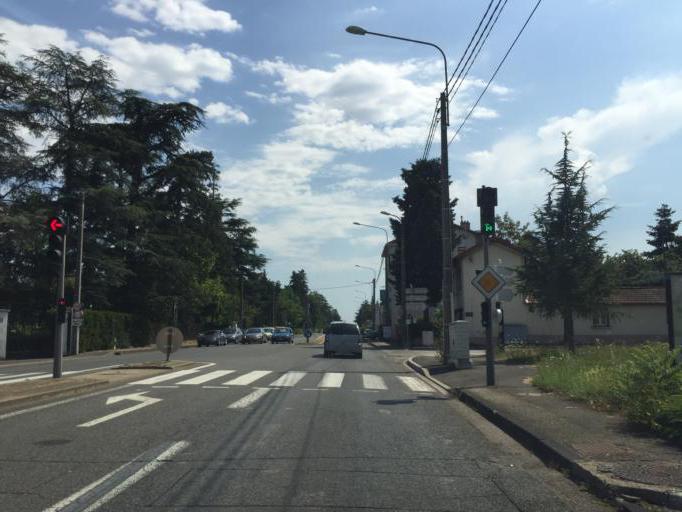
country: FR
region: Rhone-Alpes
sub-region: Departement du Rhone
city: Charbonnieres-les-Bains
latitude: 45.7788
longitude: 4.7511
